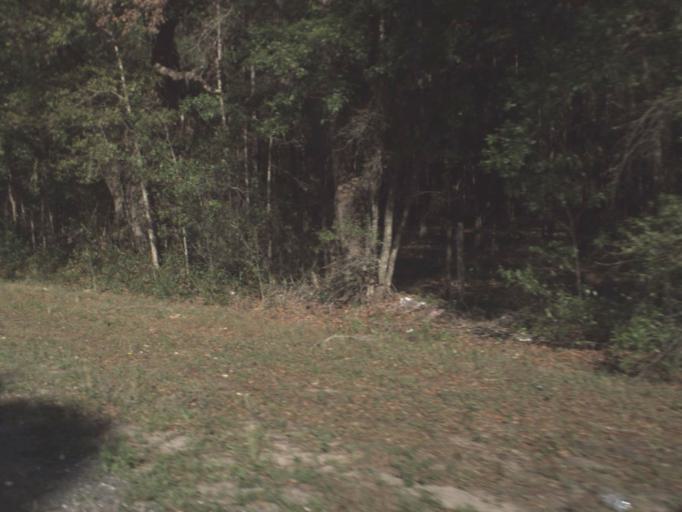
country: US
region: Florida
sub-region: Marion County
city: Dunnellon
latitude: 29.1194
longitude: -82.4357
